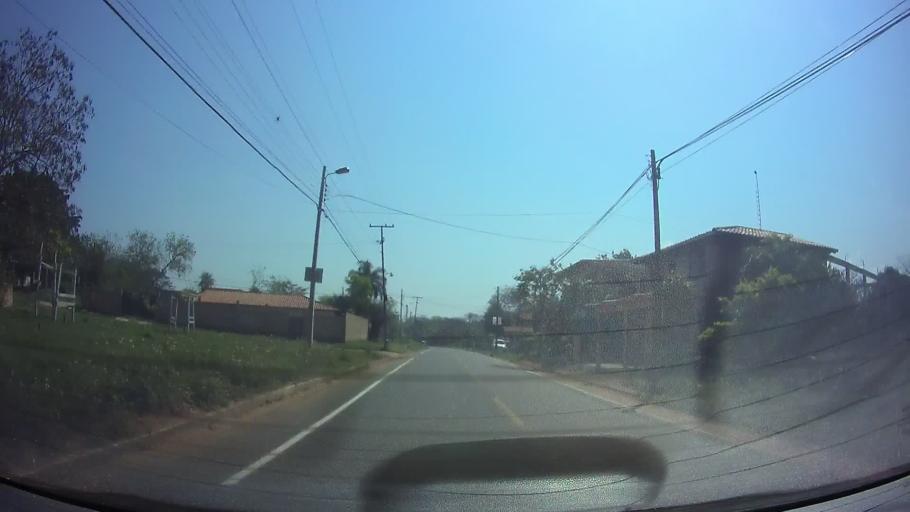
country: PY
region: Central
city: Limpio
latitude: -25.2377
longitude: -57.5039
